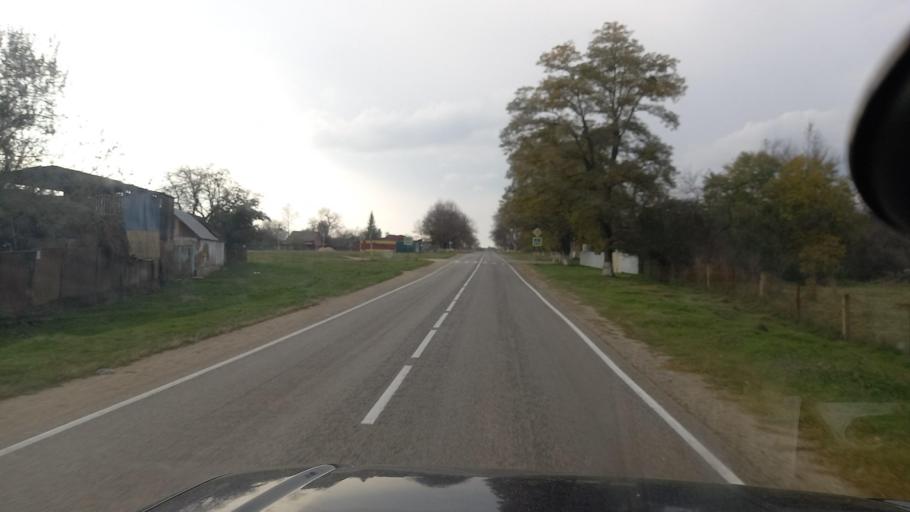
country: RU
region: Krasnodarskiy
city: Gubskaya
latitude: 44.3186
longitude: 40.6165
